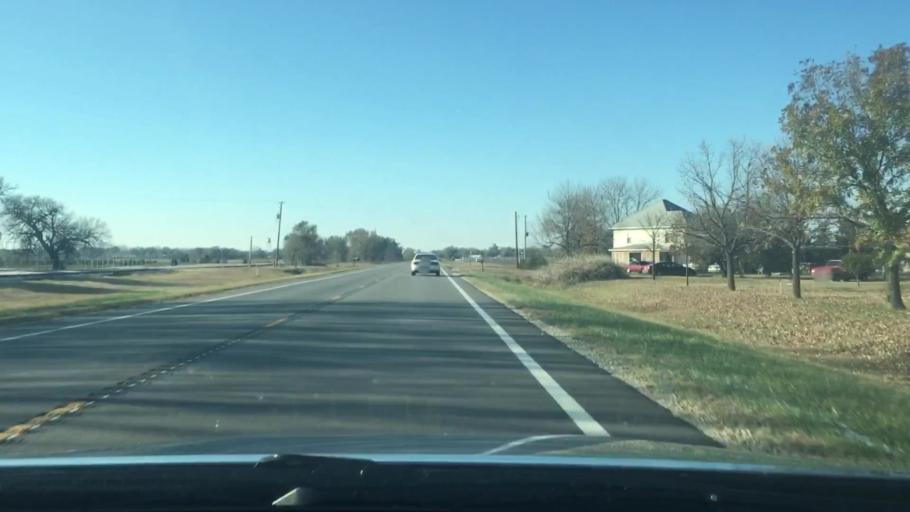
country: US
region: Kansas
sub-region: Reno County
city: Nickerson
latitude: 38.1365
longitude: -98.0677
